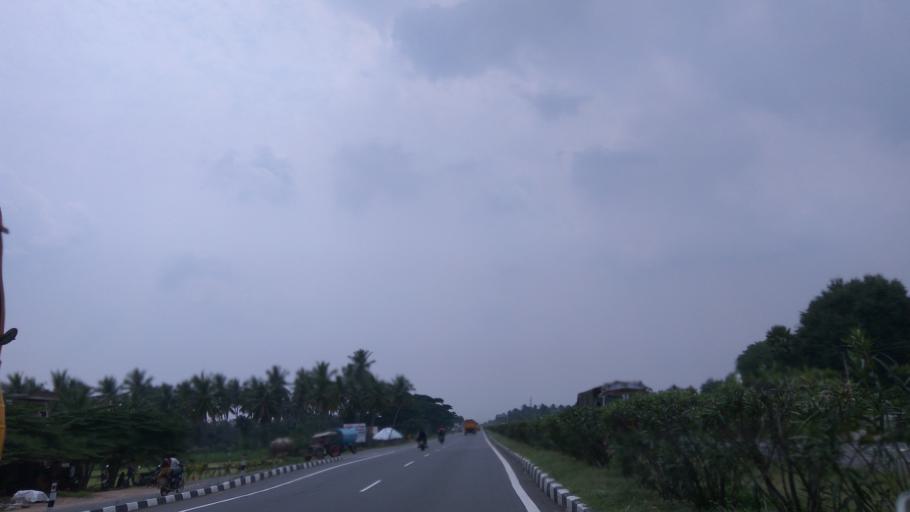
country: IN
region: Tamil Nadu
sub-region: Dharmapuri
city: Dharmapuri
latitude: 12.2400
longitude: 78.1952
